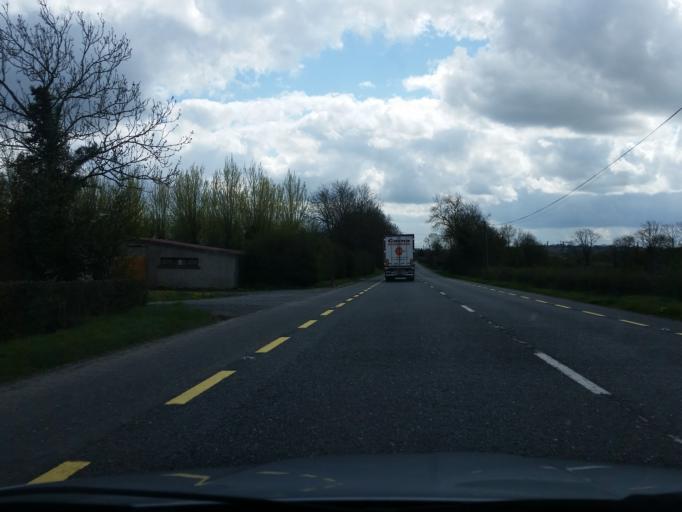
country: IE
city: Kentstown
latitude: 53.5922
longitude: -6.4643
